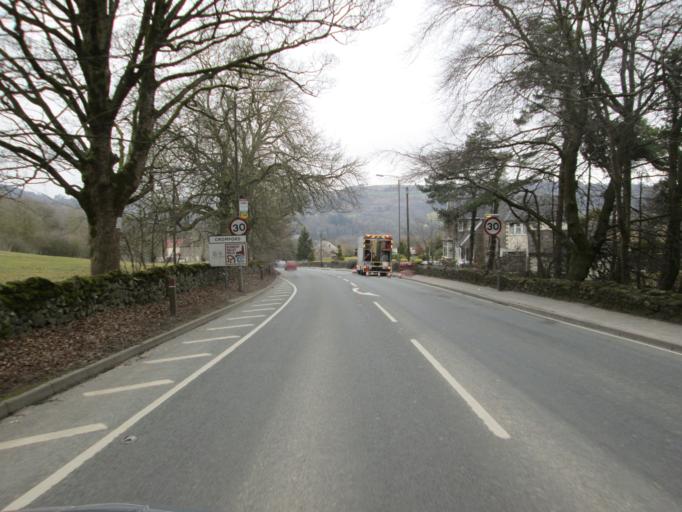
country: GB
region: England
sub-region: Derbyshire
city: Cromford
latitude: 53.1003
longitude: -1.5675
